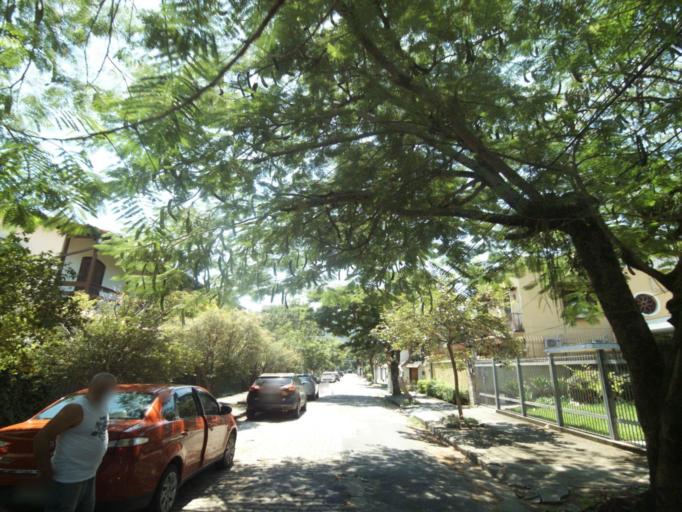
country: BR
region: Rio de Janeiro
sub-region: Niteroi
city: Niteroi
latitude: -22.9217
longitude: -43.0908
